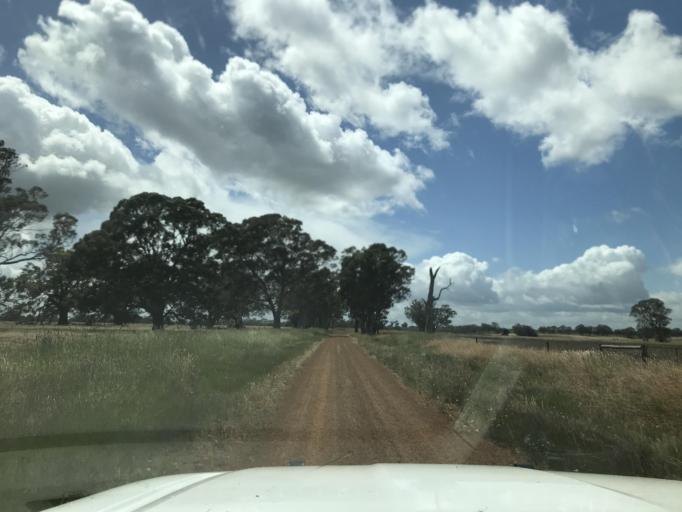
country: AU
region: South Australia
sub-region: Wattle Range
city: Penola
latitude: -37.1841
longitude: 141.4704
